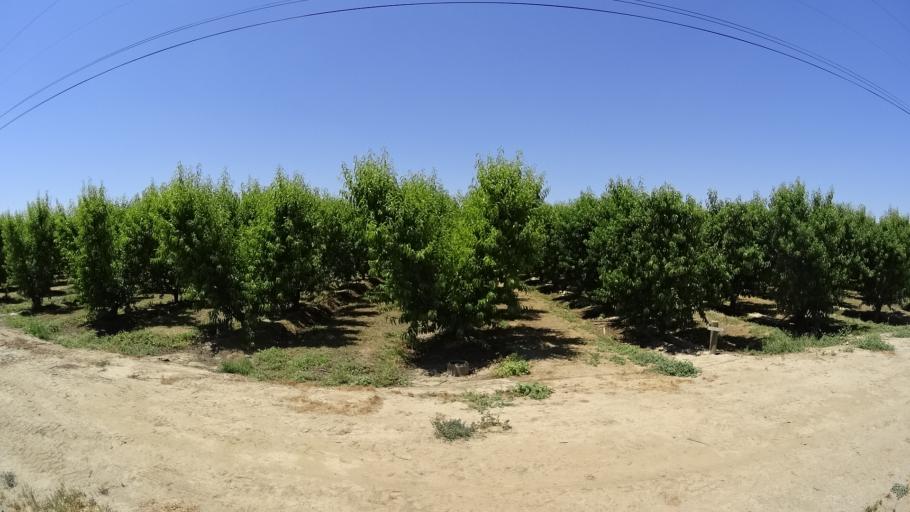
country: US
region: California
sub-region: Fresno County
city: Laton
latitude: 36.4488
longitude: -119.6095
